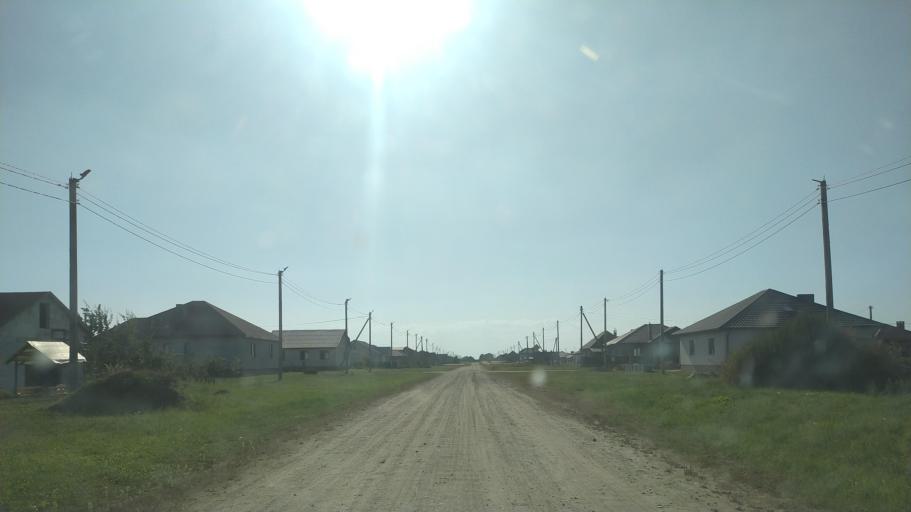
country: BY
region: Brest
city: Byaroza
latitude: 52.5165
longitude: 24.9813
